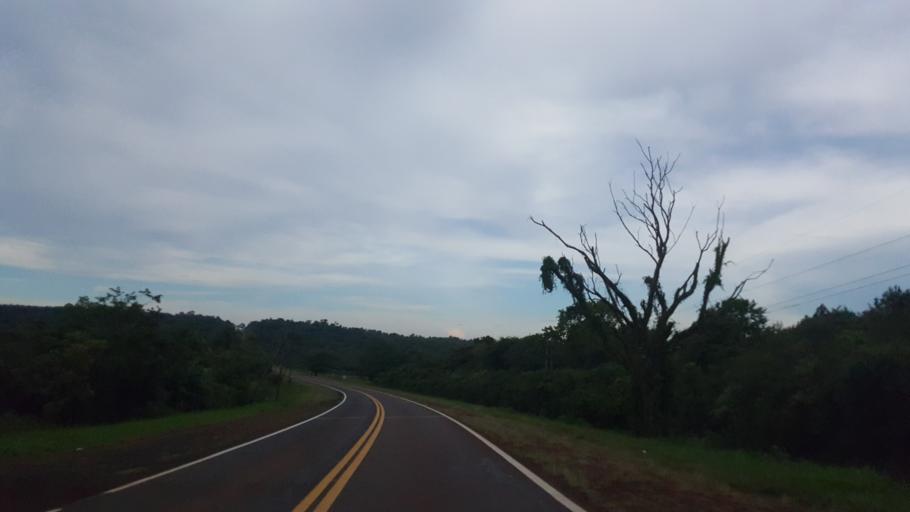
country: AR
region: Misiones
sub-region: Departamento de San Ignacio
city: San Ignacio
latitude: -27.2545
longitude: -55.5245
